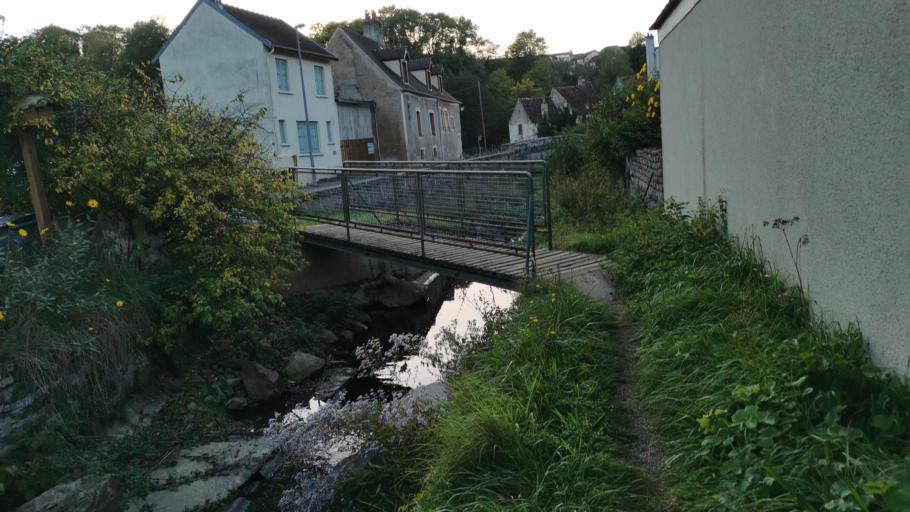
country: FR
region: Bourgogne
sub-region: Departement de la Cote-d'Or
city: Semur-en-Auxois
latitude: 47.4881
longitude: 4.3341
